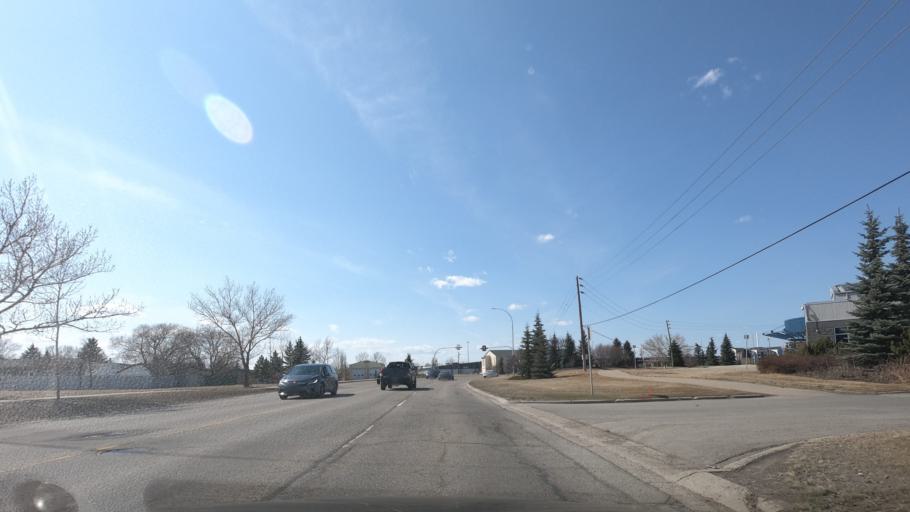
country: CA
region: Alberta
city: Airdrie
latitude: 51.2837
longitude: -113.9945
